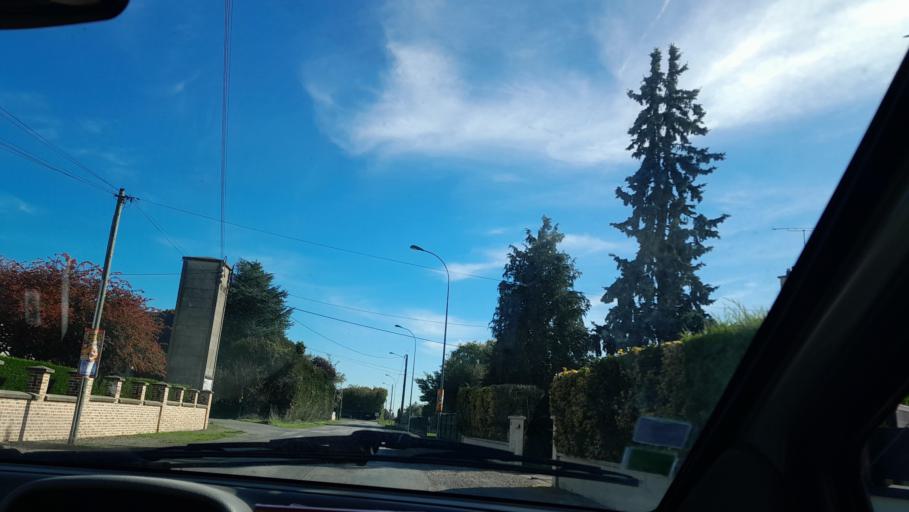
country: FR
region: Brittany
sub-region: Departement d'Ille-et-Vilaine
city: Argentre-du-Plessis
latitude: 48.0491
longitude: -1.1484
